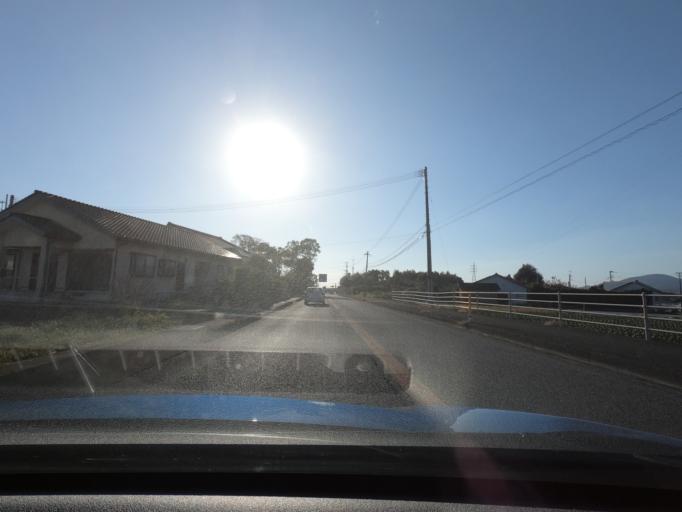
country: JP
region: Kagoshima
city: Izumi
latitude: 32.0946
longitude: 130.2976
